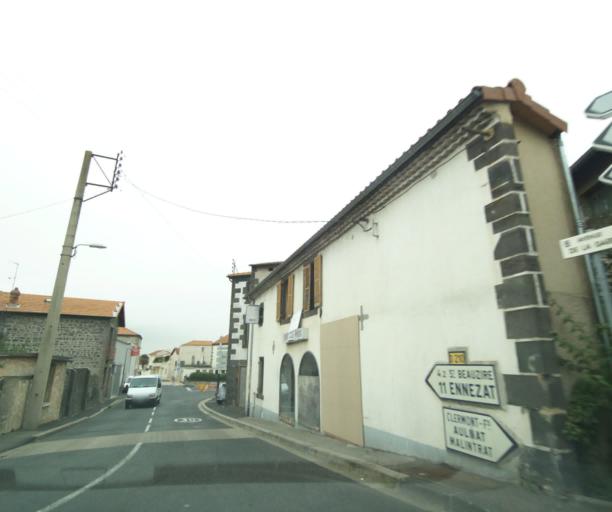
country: FR
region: Auvergne
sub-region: Departement du Puy-de-Dome
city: Gerzat
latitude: 45.8256
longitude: 3.1453
